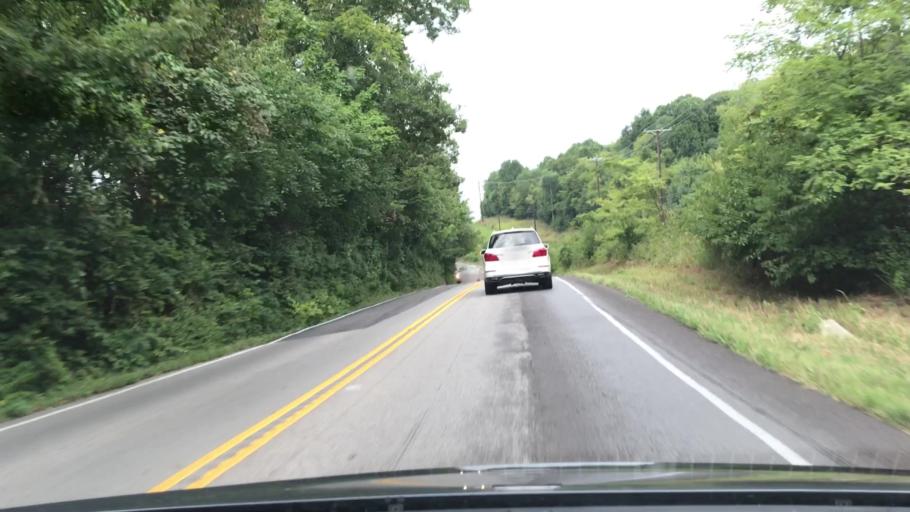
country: US
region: Tennessee
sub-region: Williamson County
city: Franklin
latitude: 35.9327
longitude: -86.7863
